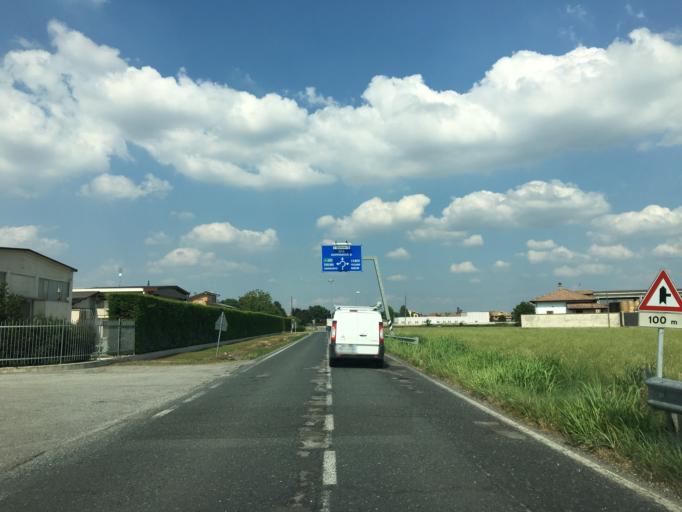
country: IT
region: Piedmont
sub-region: Provincia di Cuneo
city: Caramagna Piemonte
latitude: 44.7772
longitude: 7.7258
